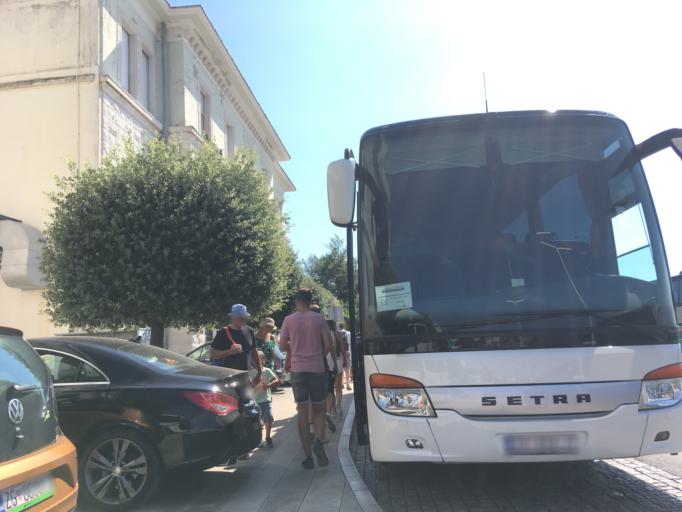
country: HR
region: Zadarska
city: Zadar
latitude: 44.1181
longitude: 15.2213
